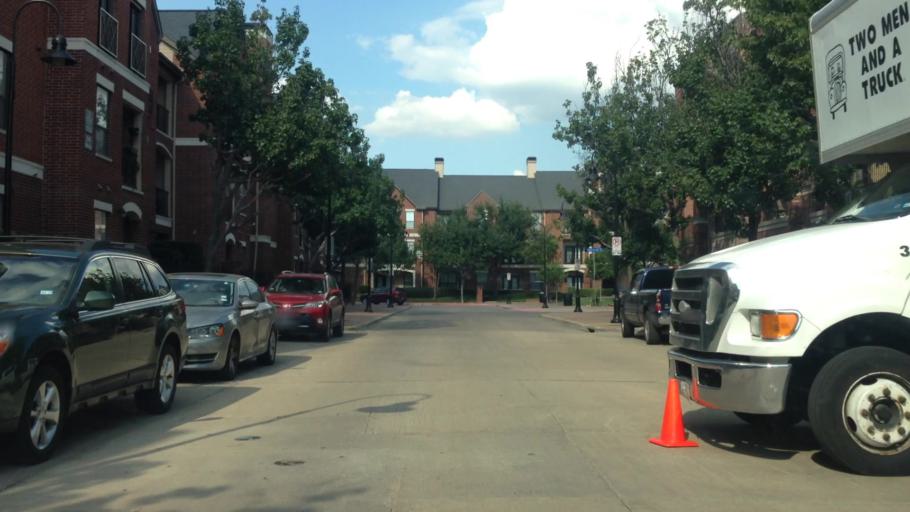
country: US
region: Texas
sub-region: Dallas County
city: Dallas
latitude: 32.7792
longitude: -96.7875
